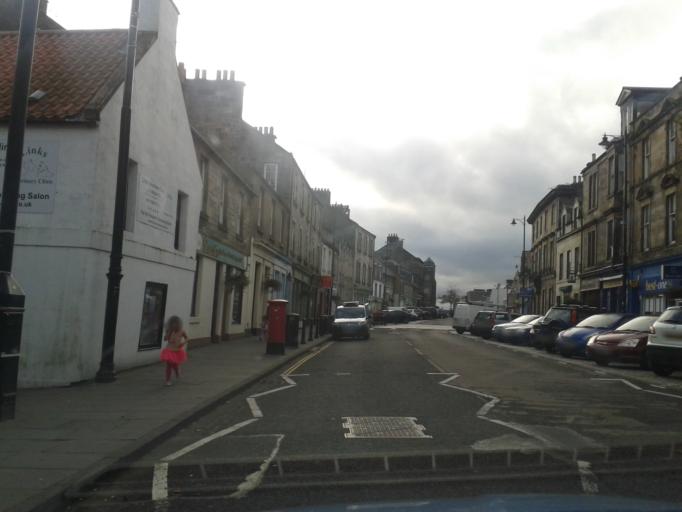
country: GB
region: Scotland
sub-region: Fife
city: Burntisland
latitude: 56.0596
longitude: -3.2315
